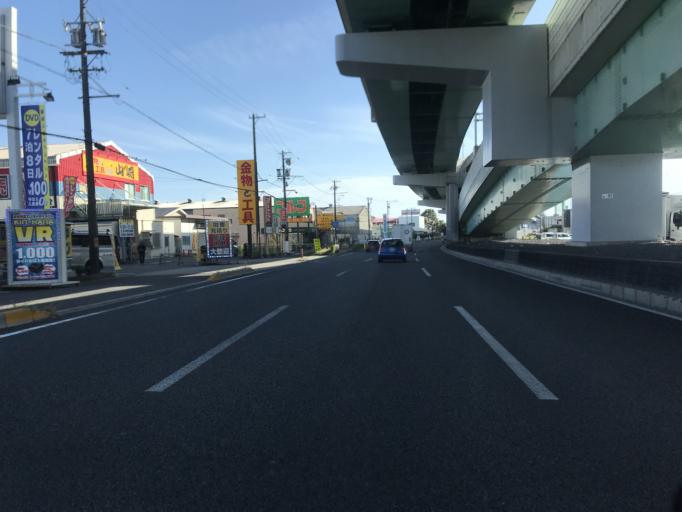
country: JP
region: Aichi
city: Iwakura
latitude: 35.2629
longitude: 136.8409
